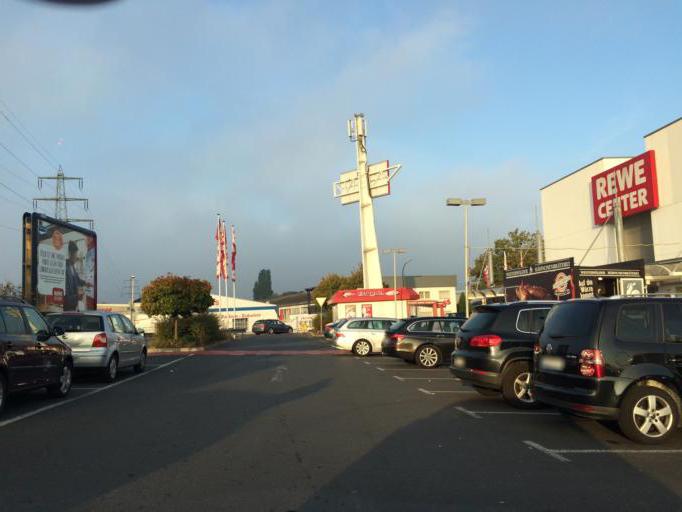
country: DE
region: North Rhine-Westphalia
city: Sankt Augustin
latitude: 50.7424
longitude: 7.1591
